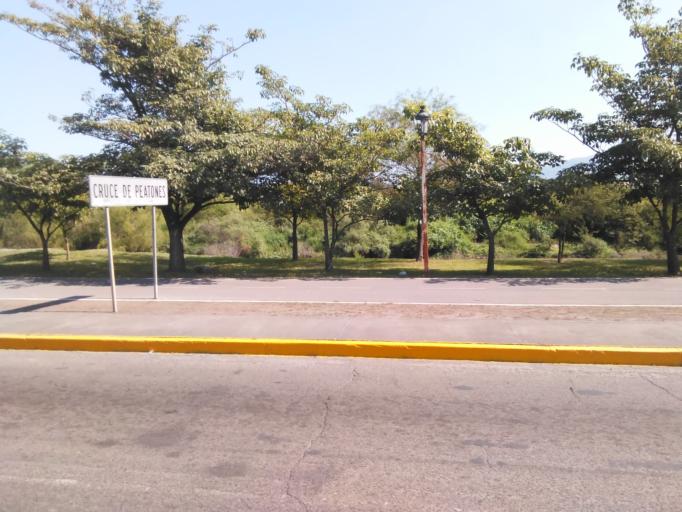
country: MX
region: Nayarit
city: Tepic
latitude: 21.4828
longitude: -104.8516
